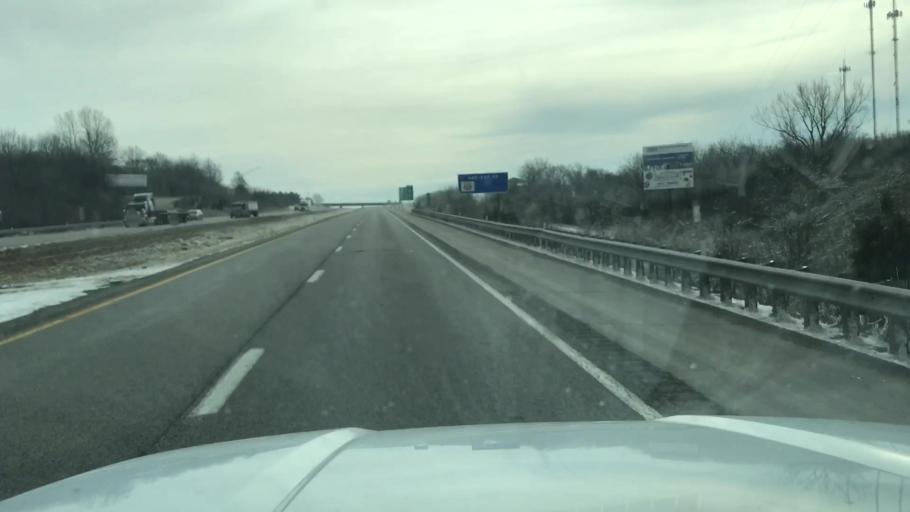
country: US
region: Missouri
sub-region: Andrew County
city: Country Club Village
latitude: 39.8626
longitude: -94.8183
